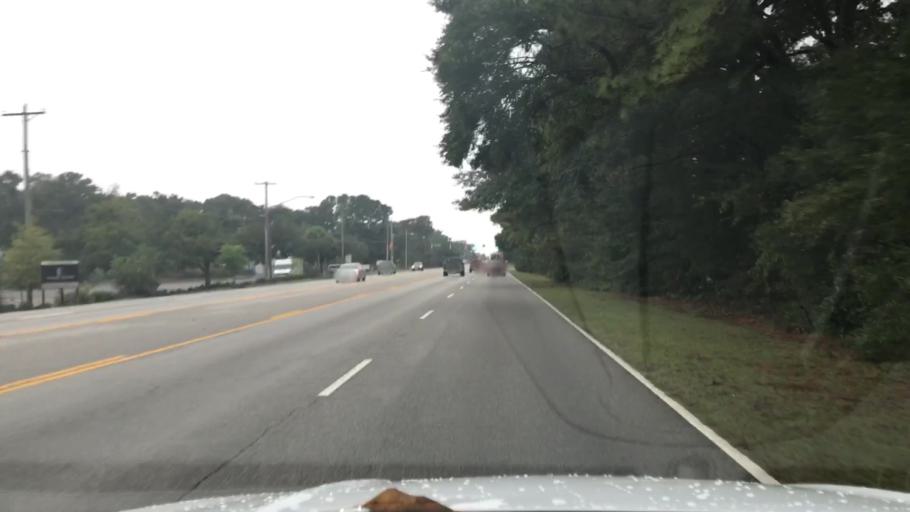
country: US
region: South Carolina
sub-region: Charleston County
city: North Charleston
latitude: 32.8141
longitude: -79.9984
